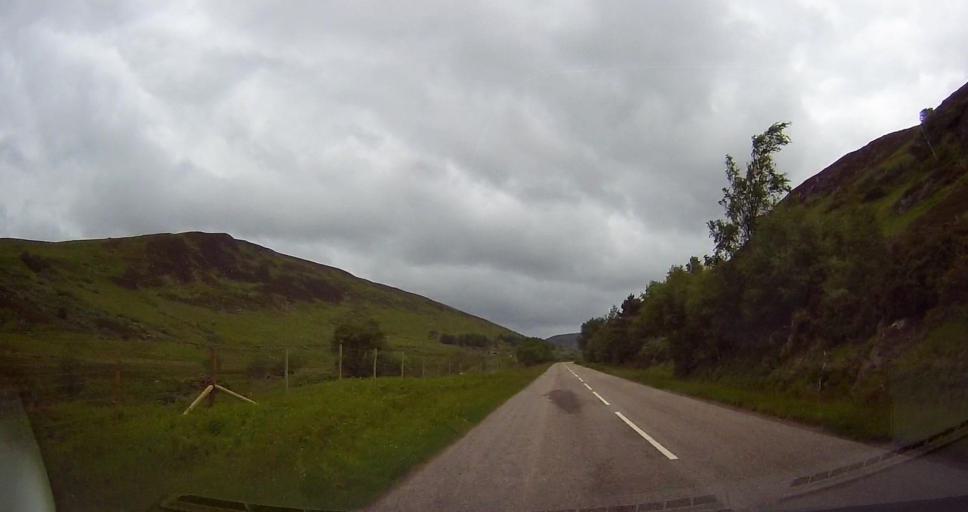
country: GB
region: Scotland
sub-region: Highland
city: Dornoch
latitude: 58.0063
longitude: -4.2659
